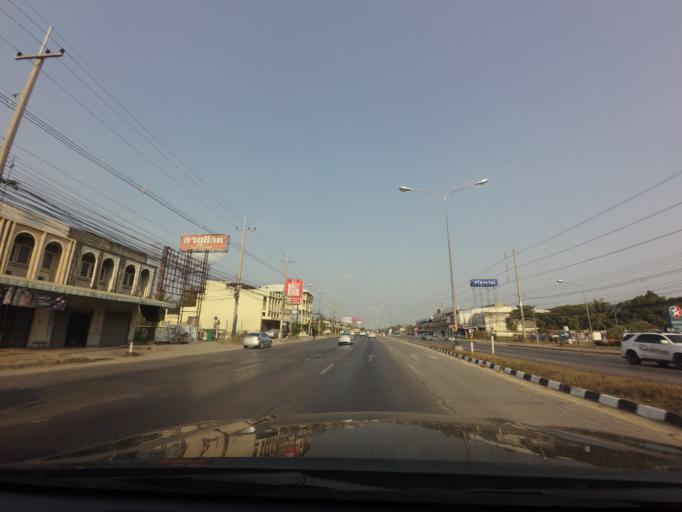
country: TH
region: Nakhon Pathom
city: Nakhon Pathom
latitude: 13.8132
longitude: 100.1051
